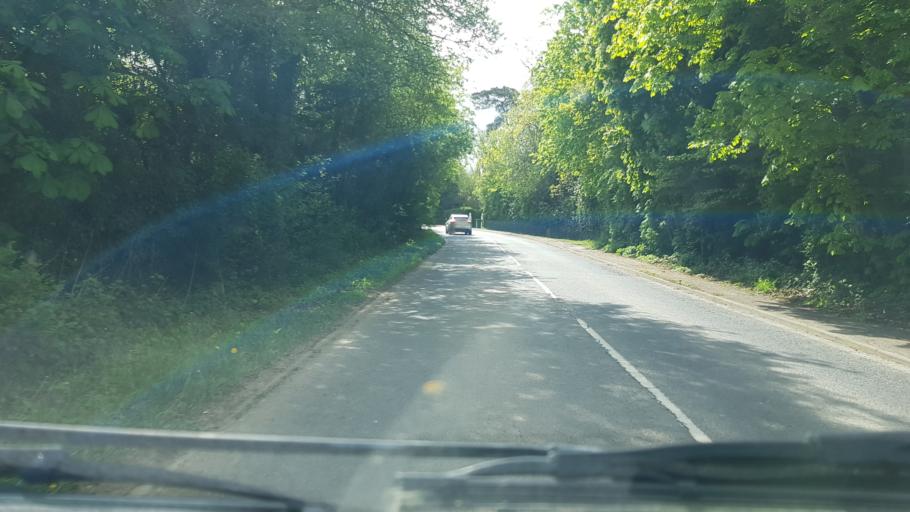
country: GB
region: England
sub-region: Surrey
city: Leatherhead
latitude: 51.3122
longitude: -0.3538
